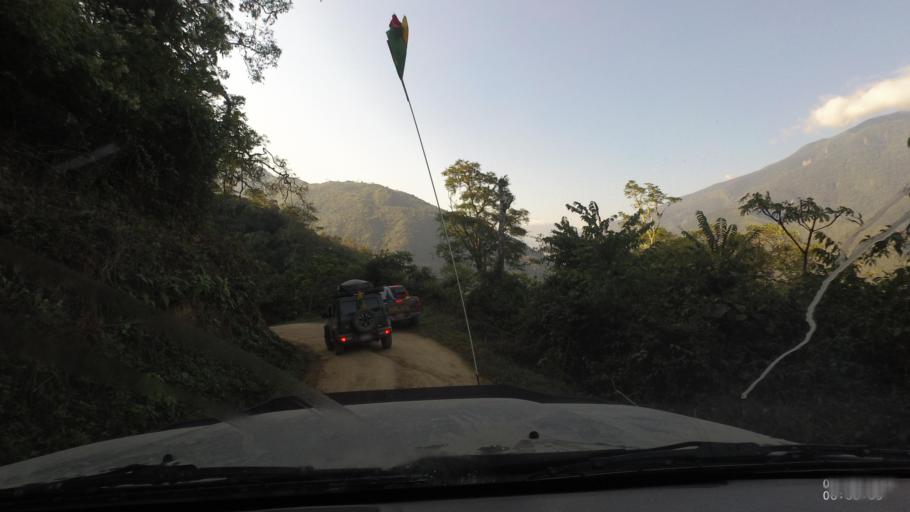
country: BO
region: La Paz
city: Quime
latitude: -16.5269
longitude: -66.7660
